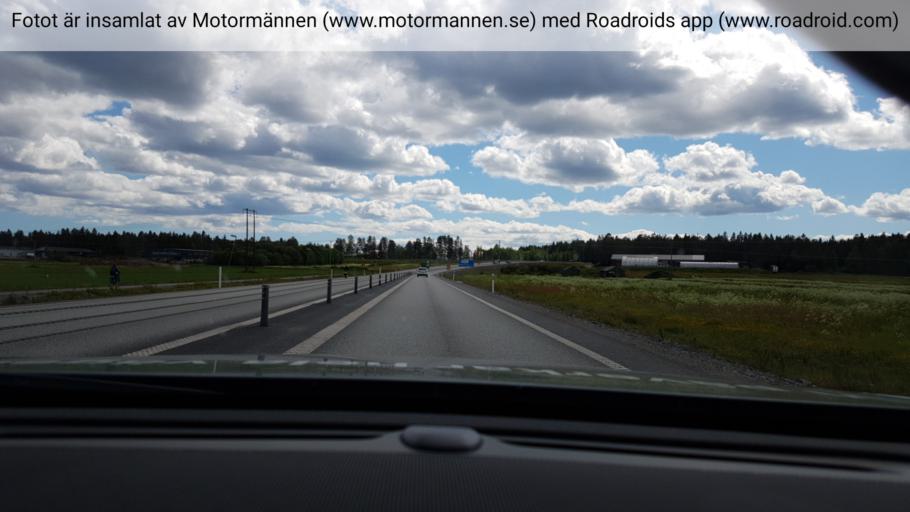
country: SE
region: Vaesterbotten
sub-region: Umea Kommun
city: Roback
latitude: 63.8469
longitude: 20.1903
